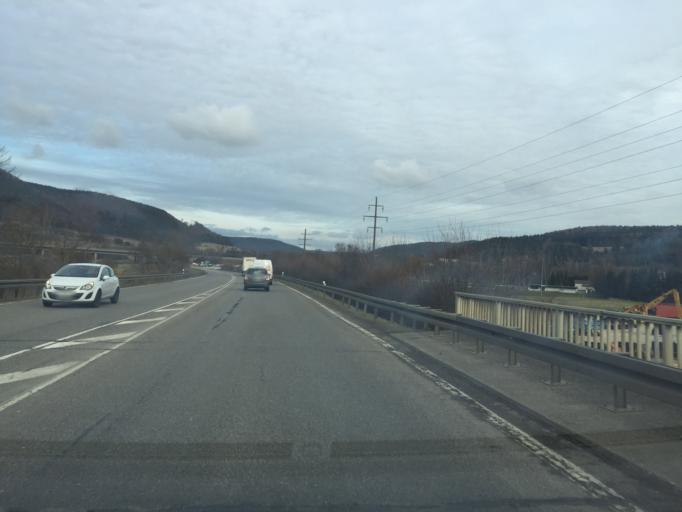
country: DE
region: Baden-Wuerttemberg
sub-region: Freiburg Region
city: Geisingen
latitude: 47.9185
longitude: 8.6669
